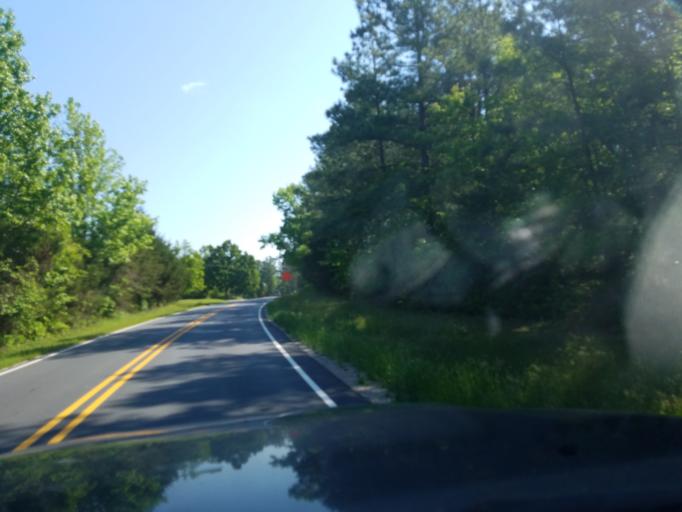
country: US
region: North Carolina
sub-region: Vance County
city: Henderson
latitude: 36.3721
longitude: -78.4476
